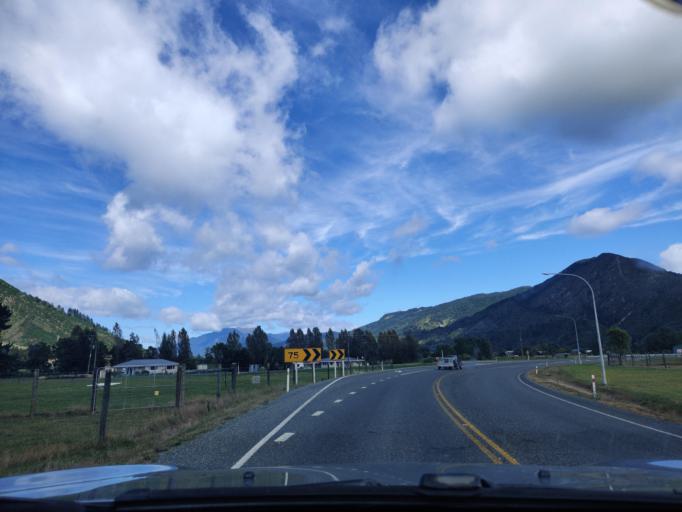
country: NZ
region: West Coast
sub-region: Buller District
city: Westport
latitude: -41.7990
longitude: 172.3372
